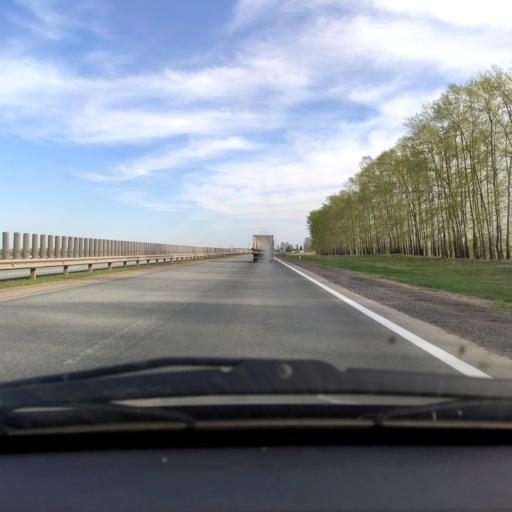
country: RU
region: Bashkortostan
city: Asanovo
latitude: 55.0077
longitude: 55.4874
